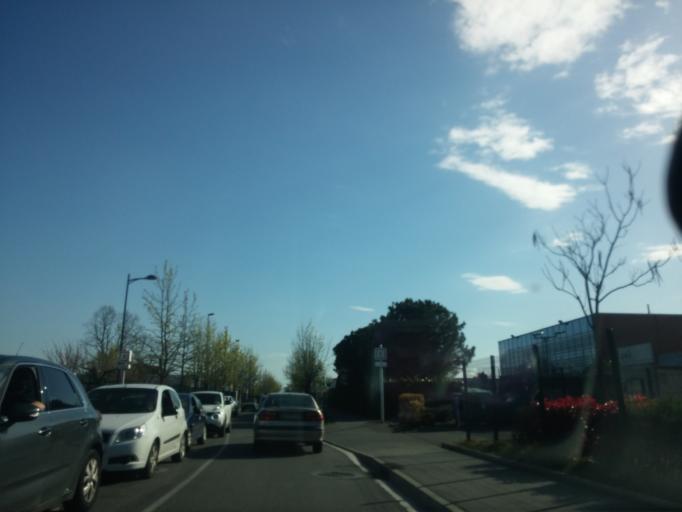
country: FR
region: Midi-Pyrenees
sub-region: Departement de la Haute-Garonne
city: Portet-sur-Garonne
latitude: 43.5699
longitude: 1.3859
